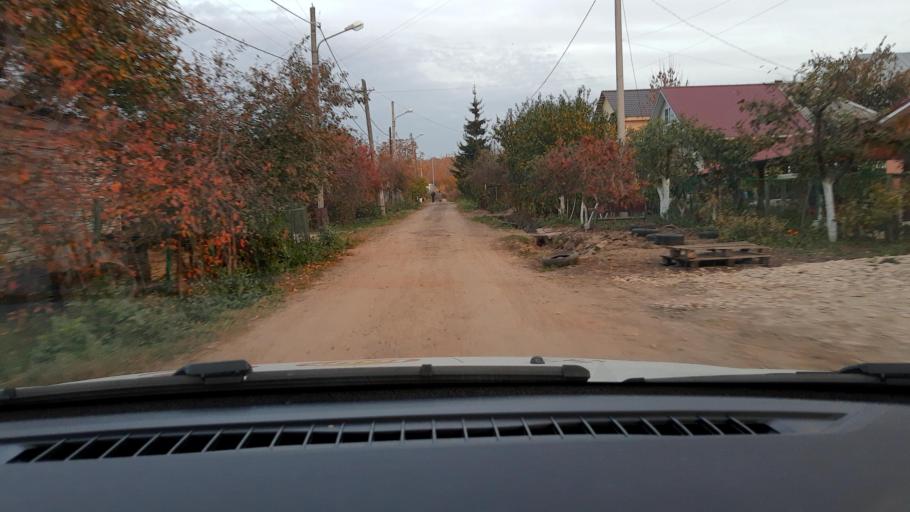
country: RU
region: Nizjnij Novgorod
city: Burevestnik
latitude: 56.2123
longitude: 43.8147
